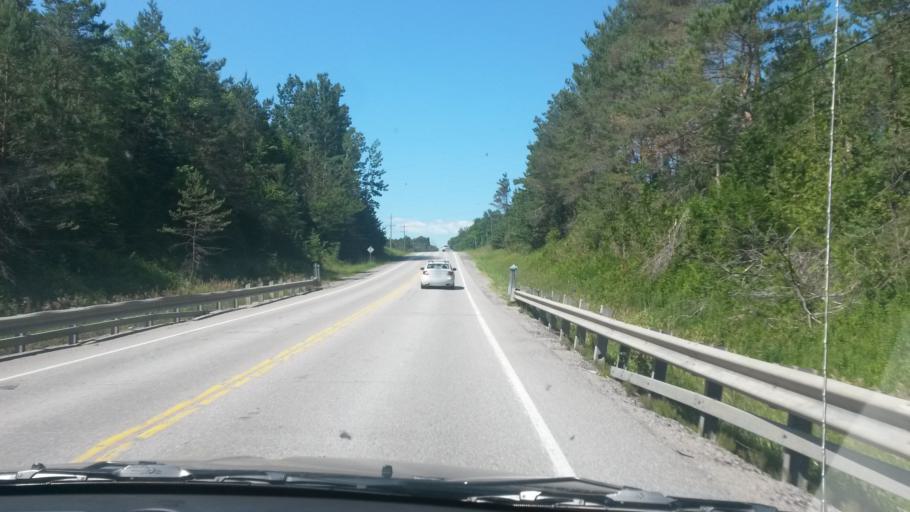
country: CA
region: Ontario
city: Barrie
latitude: 44.5124
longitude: -79.7628
